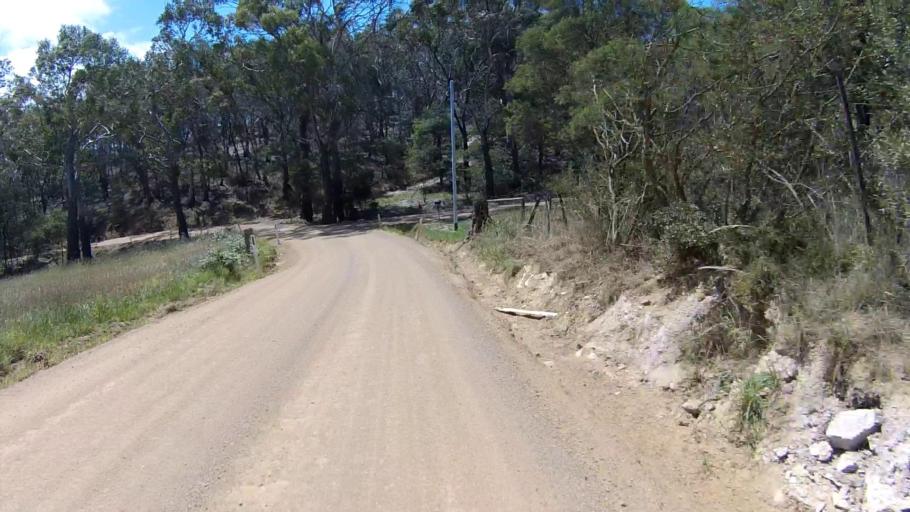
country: AU
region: Tasmania
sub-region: Clarence
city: Lauderdale
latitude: -42.9324
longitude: 147.4671
